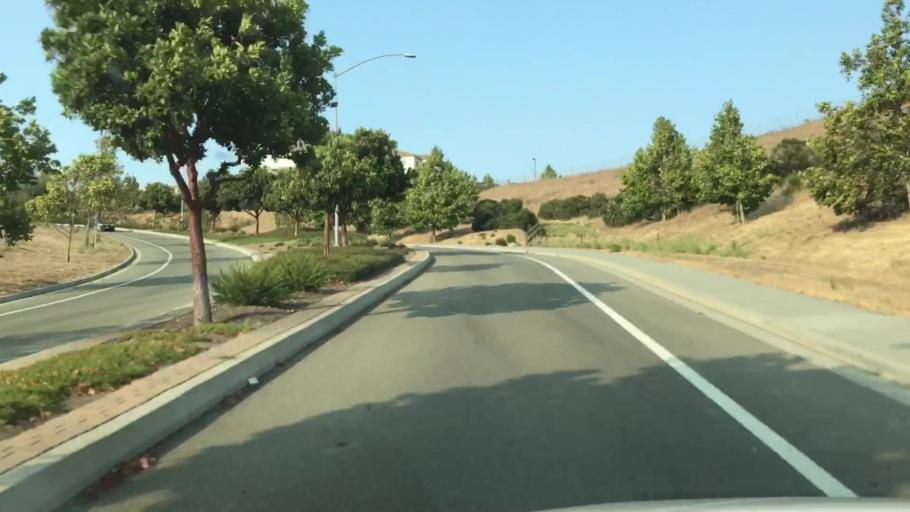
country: US
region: California
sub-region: Alameda County
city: Dublin
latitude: 37.7002
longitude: -121.9782
